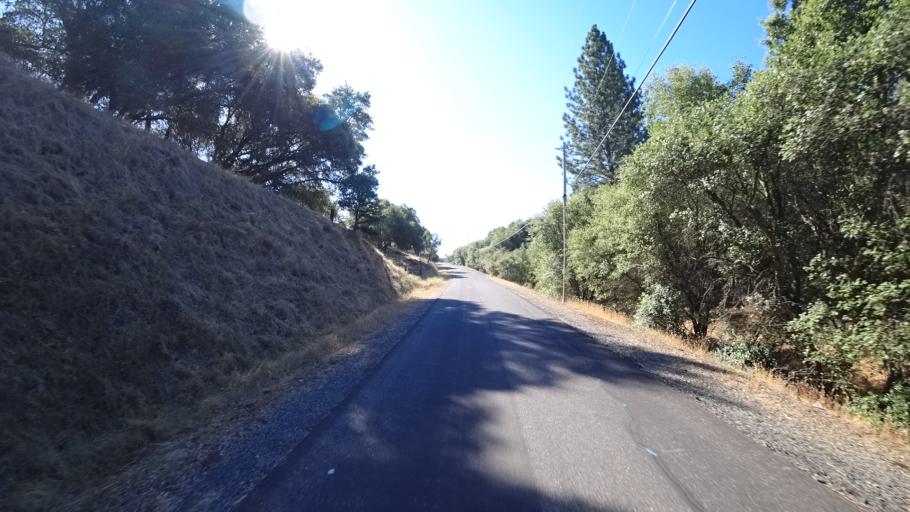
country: US
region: California
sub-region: Calaveras County
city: San Andreas
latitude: 38.2528
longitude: -120.7077
